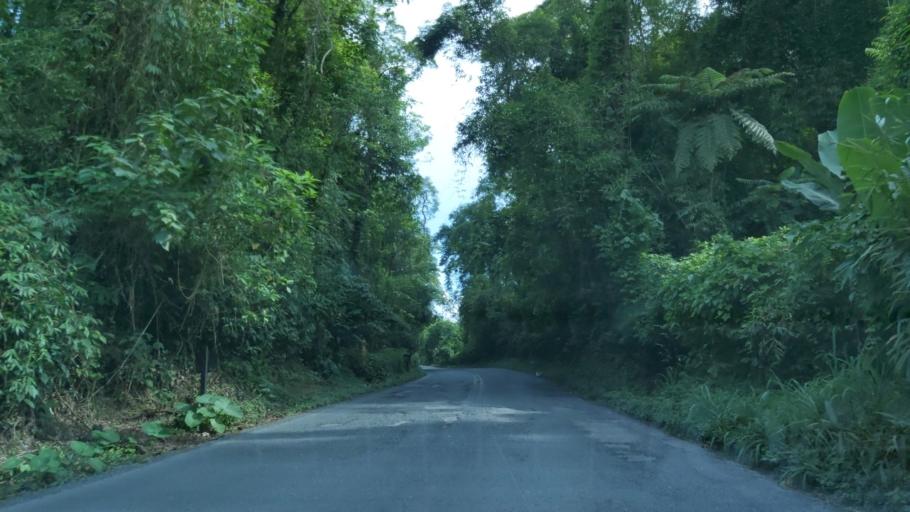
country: BR
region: Sao Paulo
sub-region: Juquia
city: Juquia
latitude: -24.0840
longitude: -47.6081
